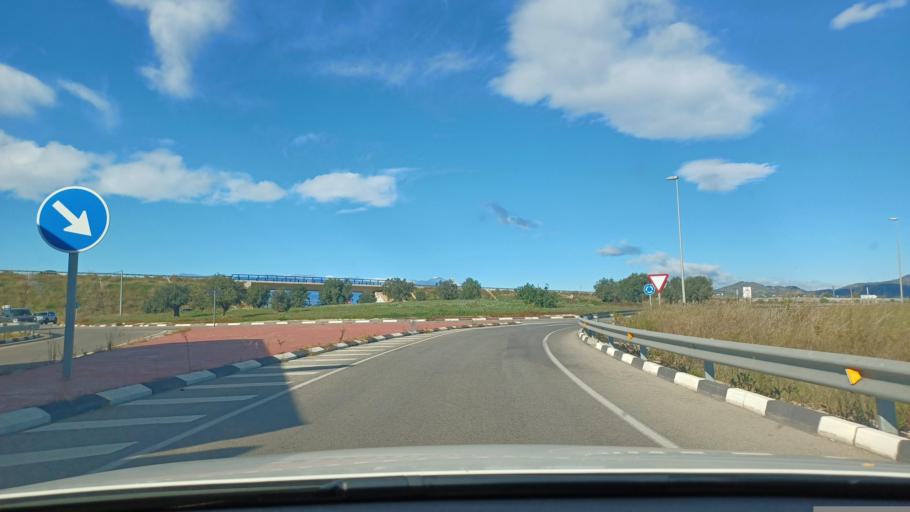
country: ES
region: Valencia
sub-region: Provincia de Castello
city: Vinaros
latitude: 40.4958
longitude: 0.4647
